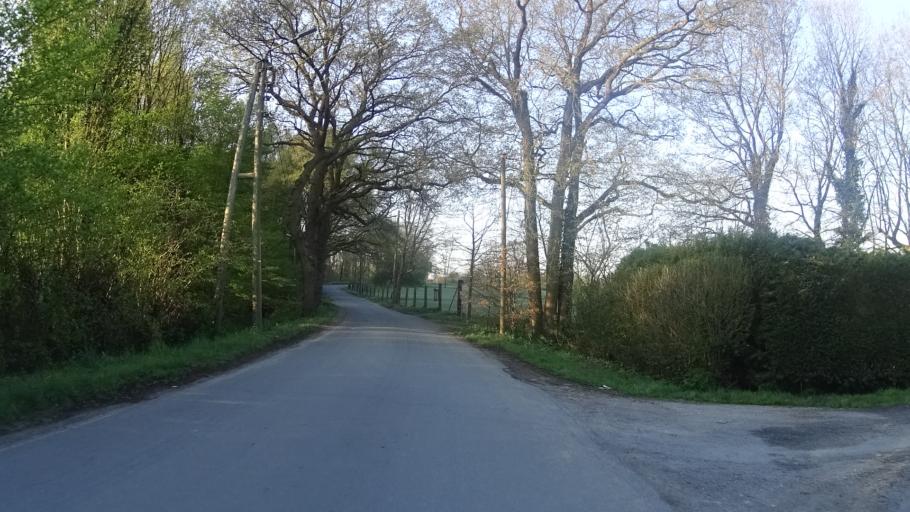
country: DE
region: North Rhine-Westphalia
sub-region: Regierungsbezirk Dusseldorf
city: Schermbeck
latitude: 51.6718
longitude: 6.8771
